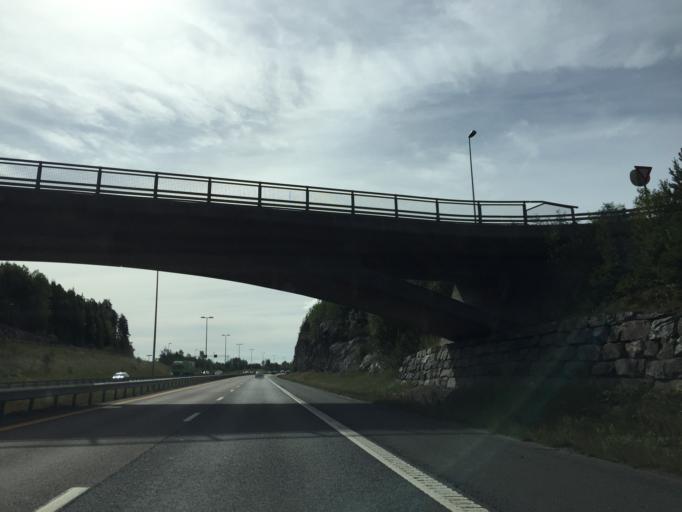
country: NO
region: Akershus
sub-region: As
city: As
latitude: 59.6897
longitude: 10.7346
